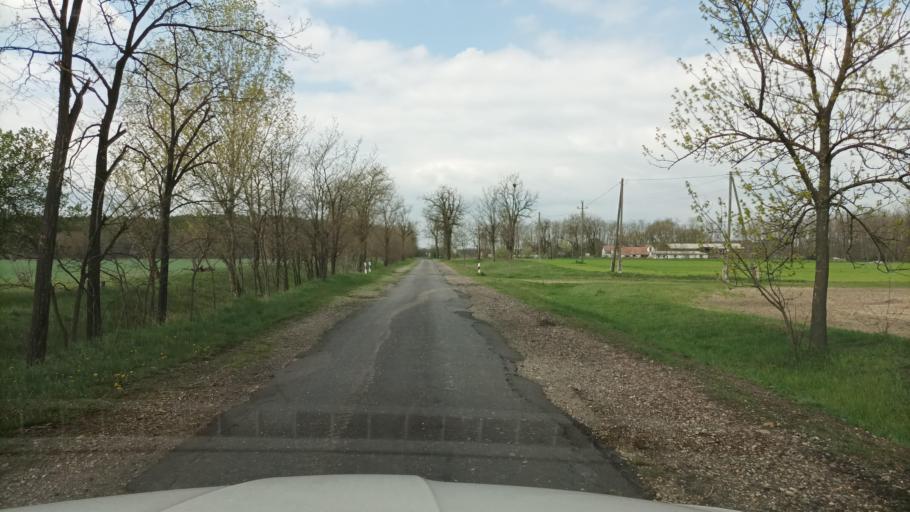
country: HU
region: Pest
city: Kocser
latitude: 47.0518
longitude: 19.8836
